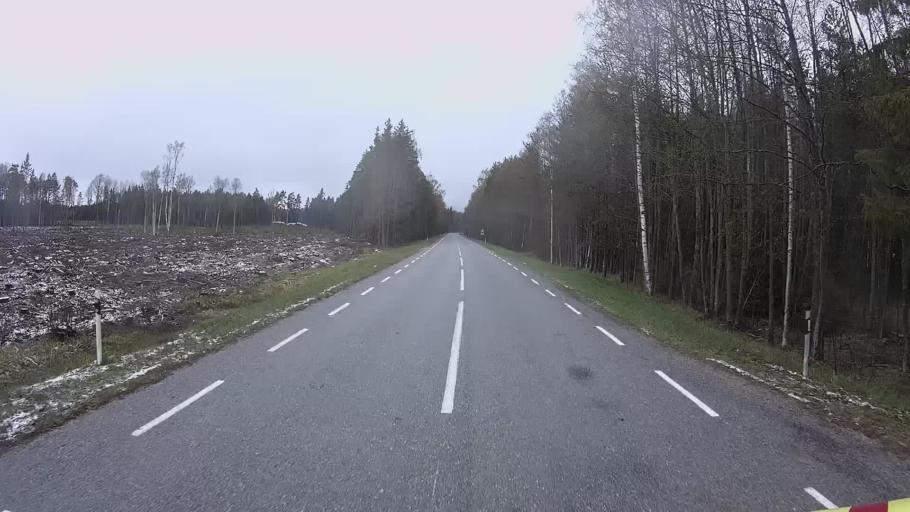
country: EE
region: Hiiumaa
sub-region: Kaerdla linn
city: Kardla
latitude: 59.0388
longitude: 22.6826
